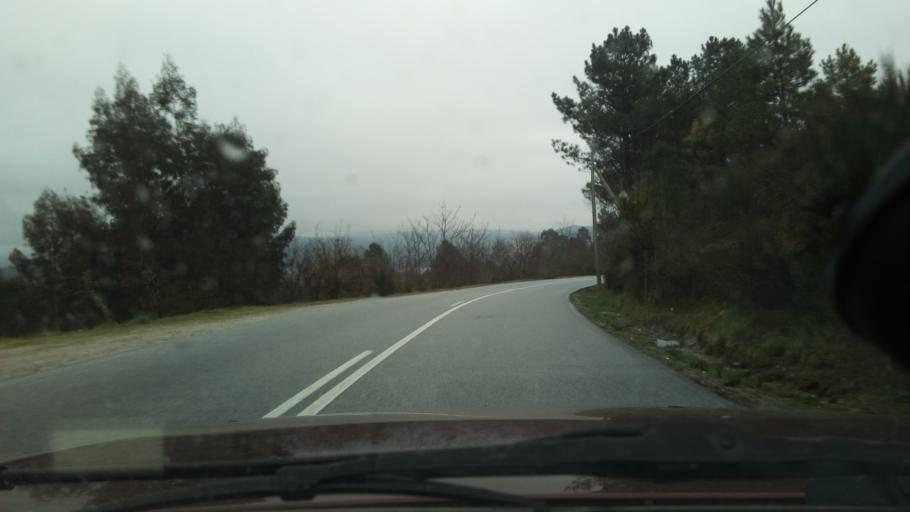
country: PT
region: Viseu
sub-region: Mangualde
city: Mangualde
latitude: 40.6112
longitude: -7.6969
